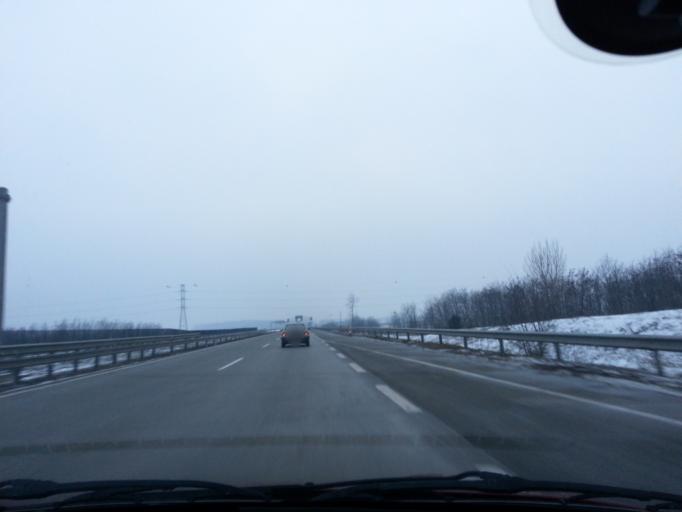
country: HU
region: Pest
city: Gyal
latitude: 47.3755
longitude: 19.2583
